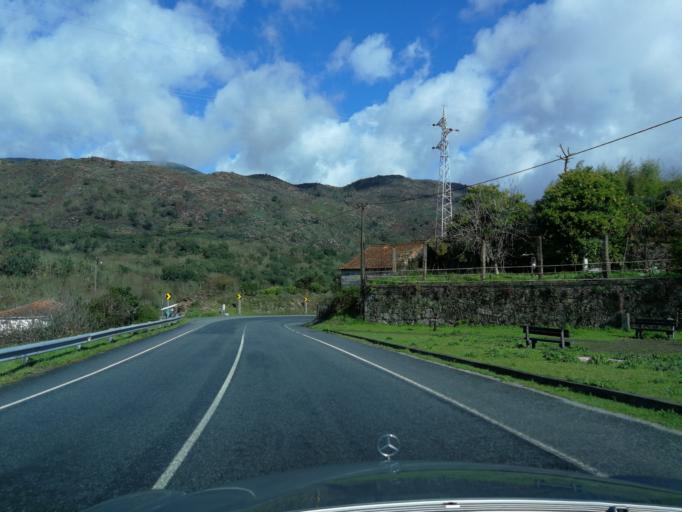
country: PT
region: Braga
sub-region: Terras de Bouro
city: Antas
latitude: 41.8366
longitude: -8.2953
